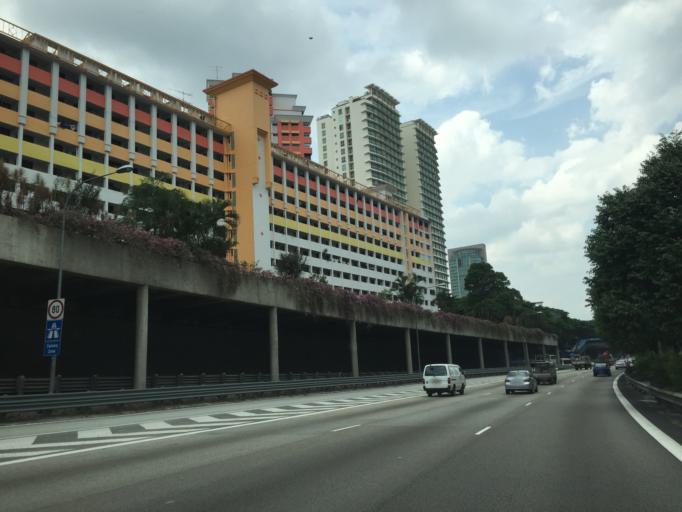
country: SG
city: Singapore
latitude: 1.3295
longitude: 103.8421
